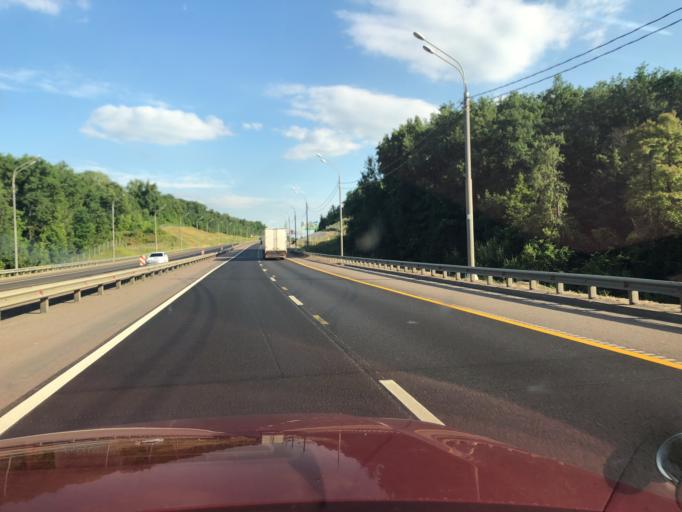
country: RU
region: Lipetsk
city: Zadonsk
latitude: 52.4046
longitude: 38.8560
